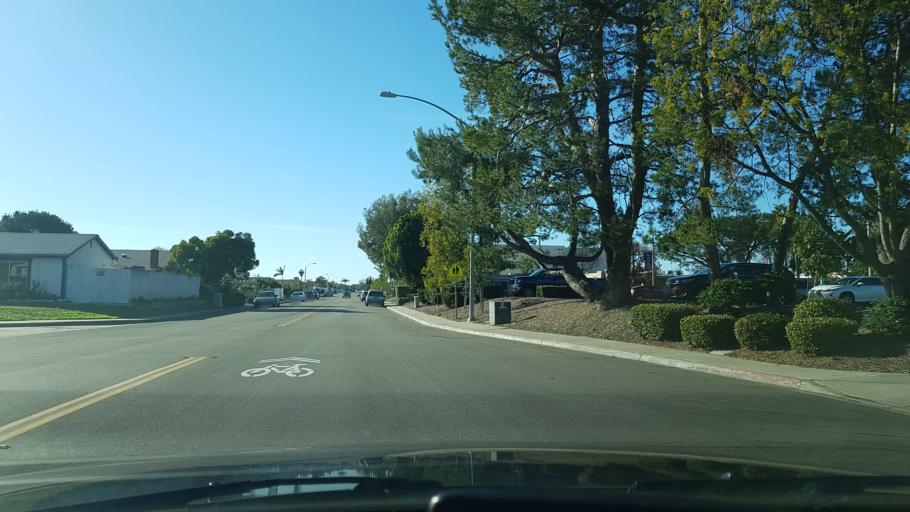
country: US
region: California
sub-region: San Diego County
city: Fairbanks Ranch
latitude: 32.9054
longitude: -117.1468
